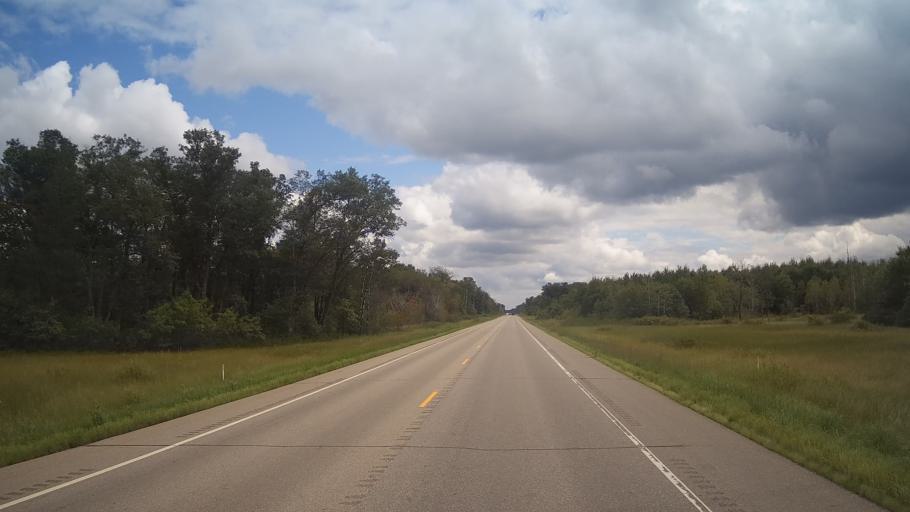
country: US
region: Wisconsin
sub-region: Adams County
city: Friendship
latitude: 44.0252
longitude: -89.7382
